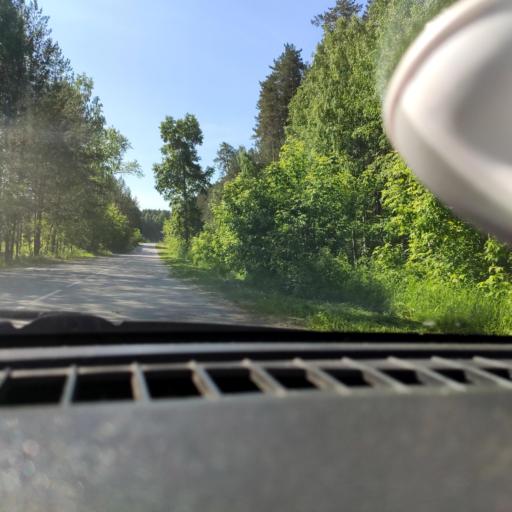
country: RU
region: Perm
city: Overyata
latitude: 57.9974
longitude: 55.8812
